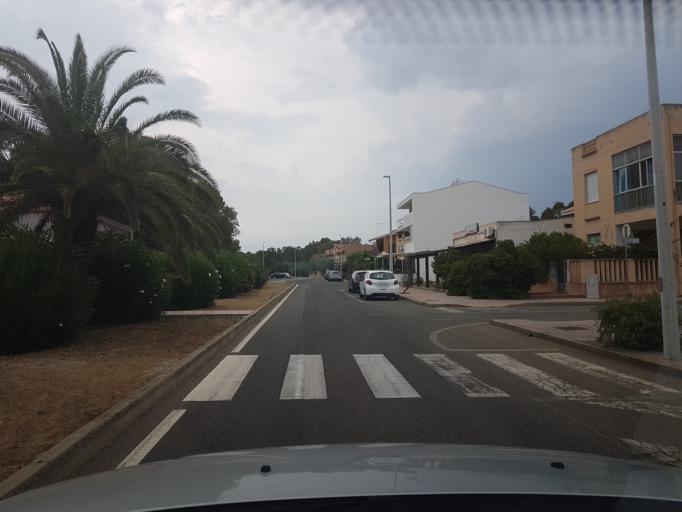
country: IT
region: Sardinia
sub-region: Provincia di Oristano
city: Cabras
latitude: 39.9084
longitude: 8.5111
